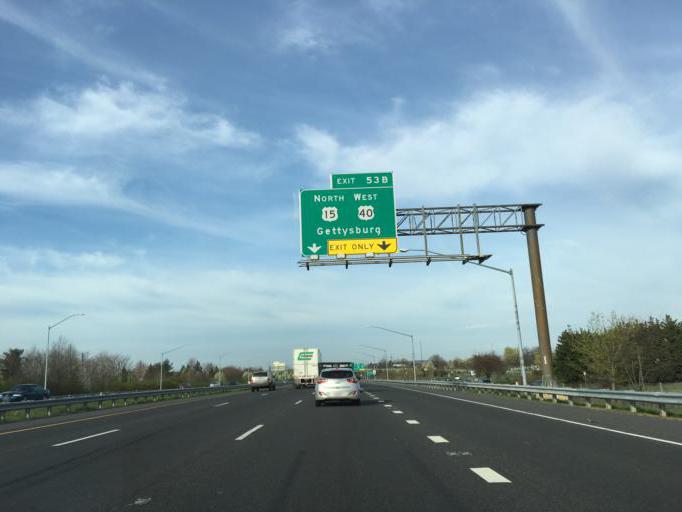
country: US
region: Maryland
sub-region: Frederick County
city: Frederick
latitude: 39.3993
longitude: -77.4125
